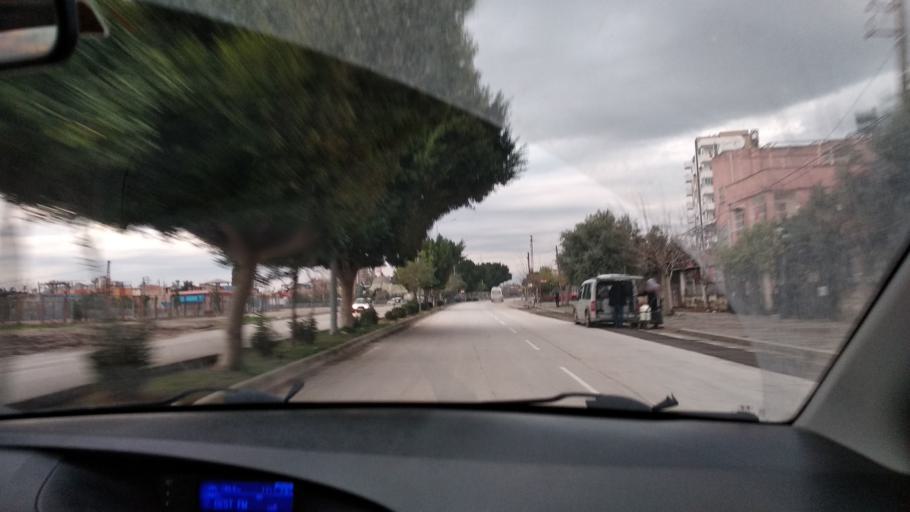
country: TR
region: Adana
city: Yuregir
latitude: 37.0105
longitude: 35.3896
